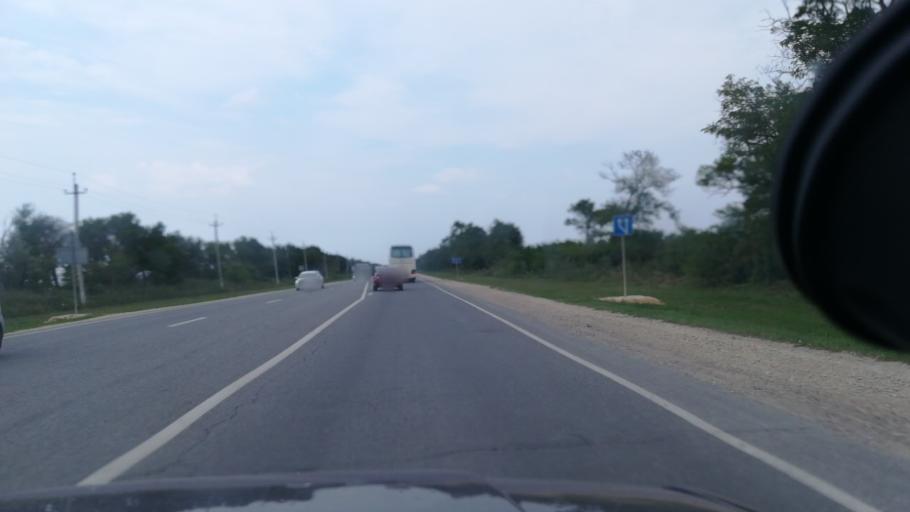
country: RU
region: Krasnodarskiy
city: Tsibanobalka
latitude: 44.9866
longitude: 37.3219
